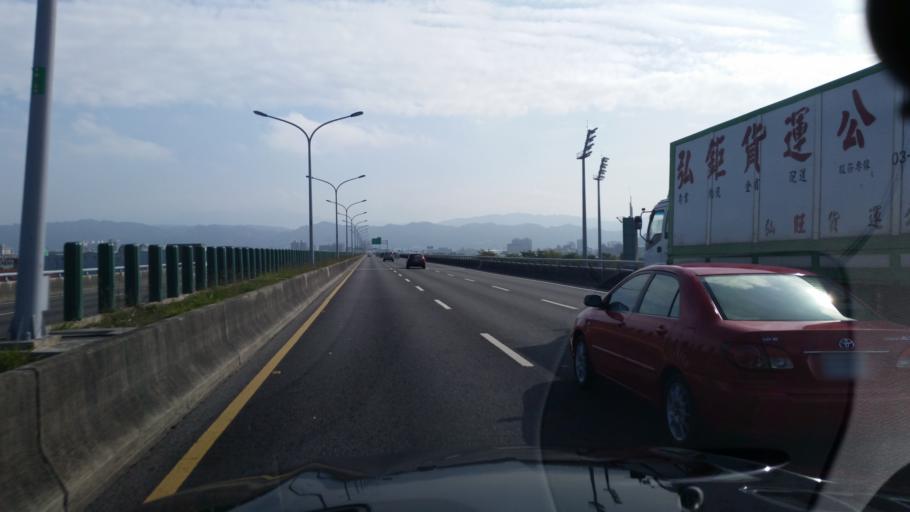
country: TW
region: Taiwan
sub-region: Taichung City
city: Taichung
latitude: 24.2010
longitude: 120.6835
